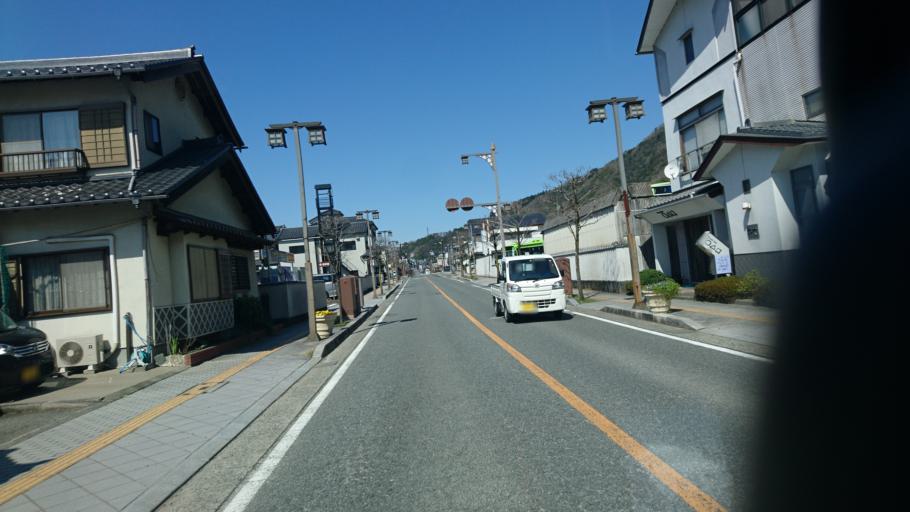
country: JP
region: Shizuoka
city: Fujinomiya
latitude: 35.3596
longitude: 138.4522
